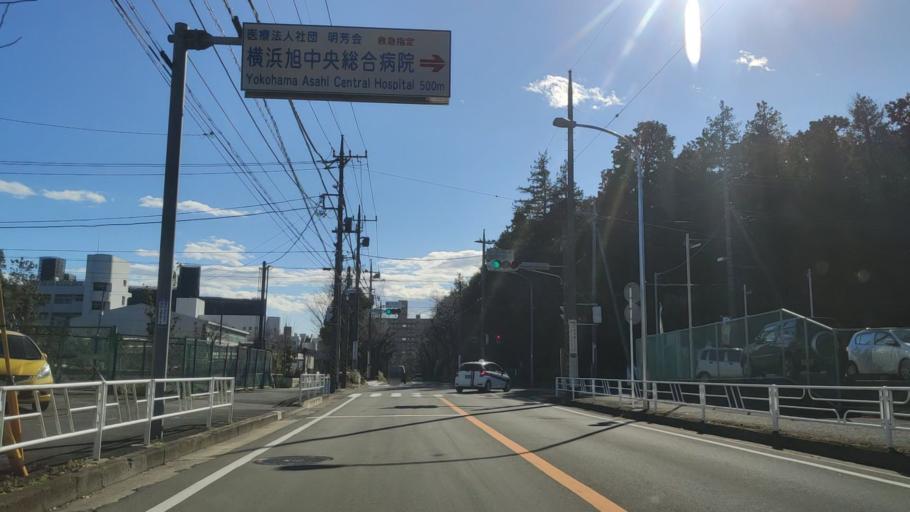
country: JP
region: Kanagawa
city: Minami-rinkan
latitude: 35.5095
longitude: 139.5030
